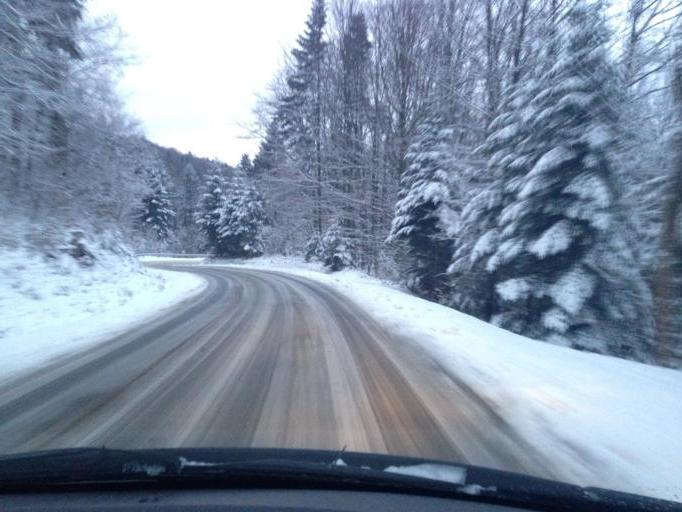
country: PL
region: Subcarpathian Voivodeship
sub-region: Powiat jasielski
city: Krempna
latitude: 49.5319
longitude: 21.5003
